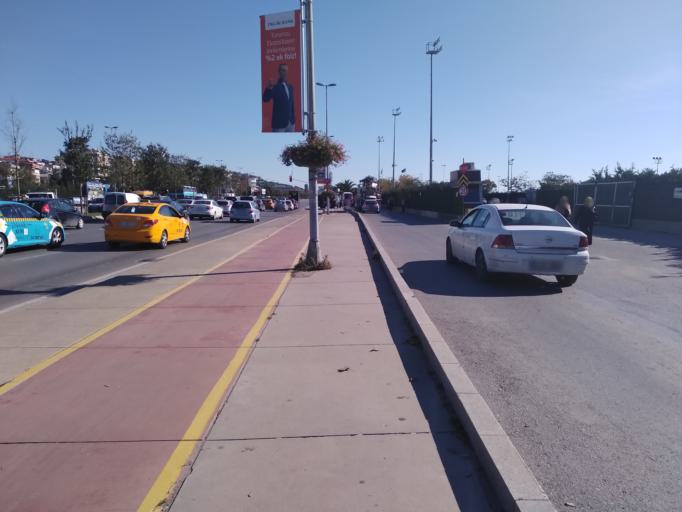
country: TR
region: Istanbul
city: Maltepe
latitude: 40.9187
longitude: 29.1292
